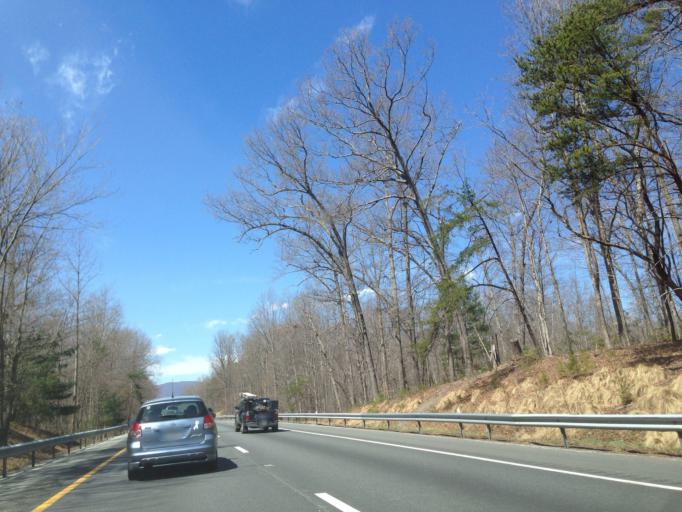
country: US
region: Virginia
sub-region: Albemarle County
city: Crozet
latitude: 38.0338
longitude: -78.6888
